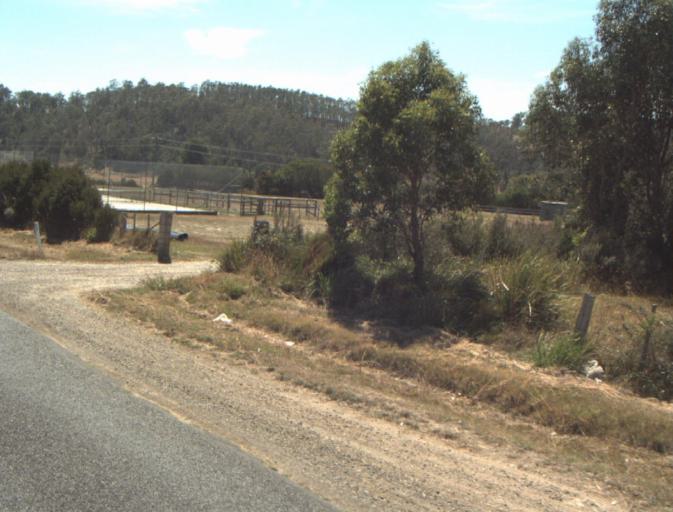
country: AU
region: Tasmania
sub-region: Launceston
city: Mayfield
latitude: -41.2546
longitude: 147.1468
